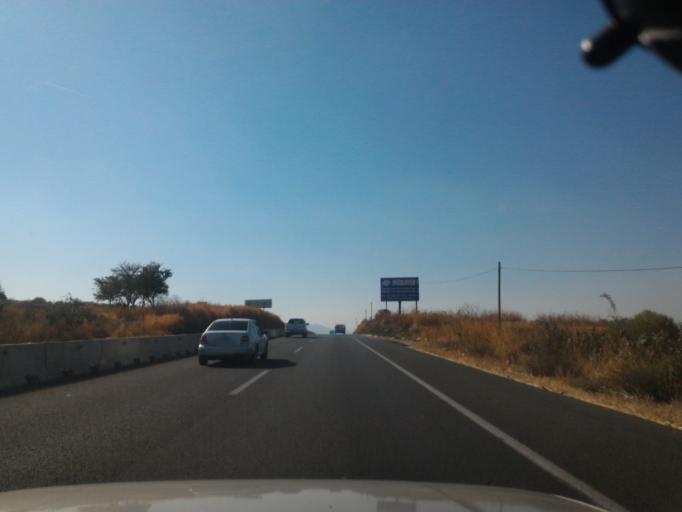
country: MX
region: Jalisco
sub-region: Poncitlan
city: Cuitzeo (La Estancia)
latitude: 20.3653
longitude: -102.8182
